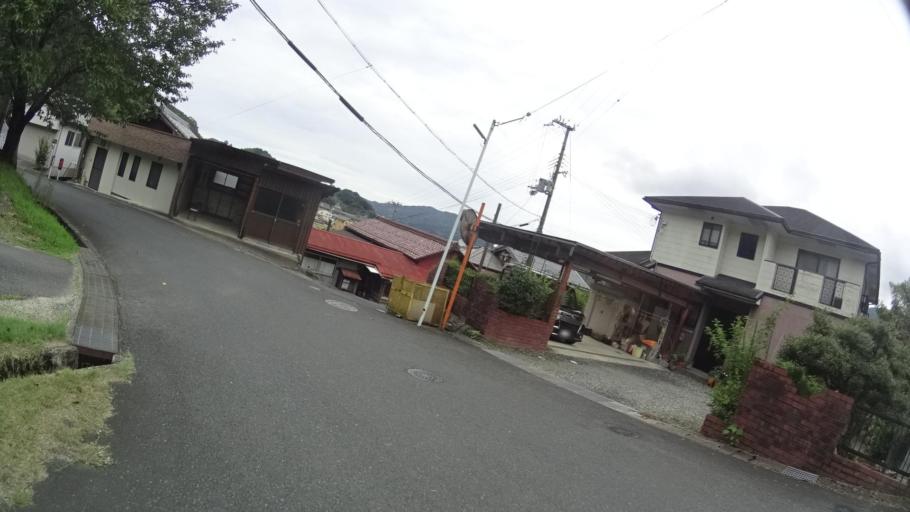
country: JP
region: Kyoto
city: Miyazu
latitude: 35.5270
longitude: 135.1853
